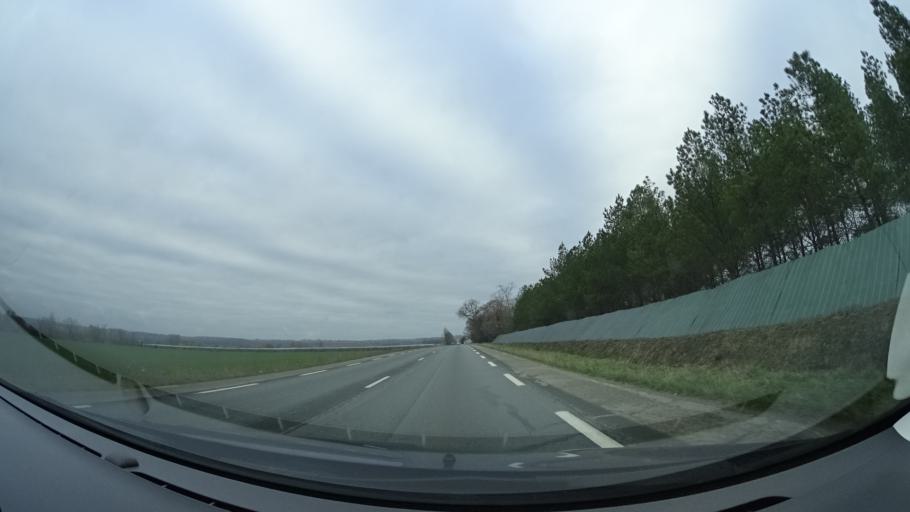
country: FR
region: Aquitaine
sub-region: Departement du Lot-et-Garonne
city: Damazan
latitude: 44.2899
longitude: 0.3064
